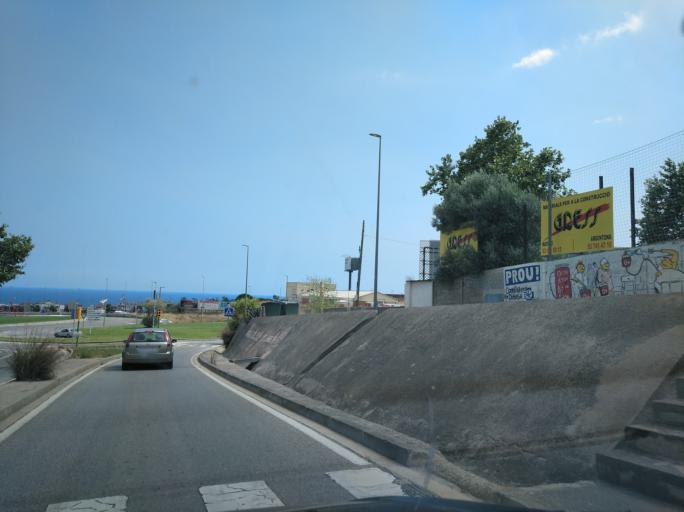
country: ES
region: Catalonia
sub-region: Provincia de Barcelona
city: Mataro
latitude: 41.5544
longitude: 2.4299
